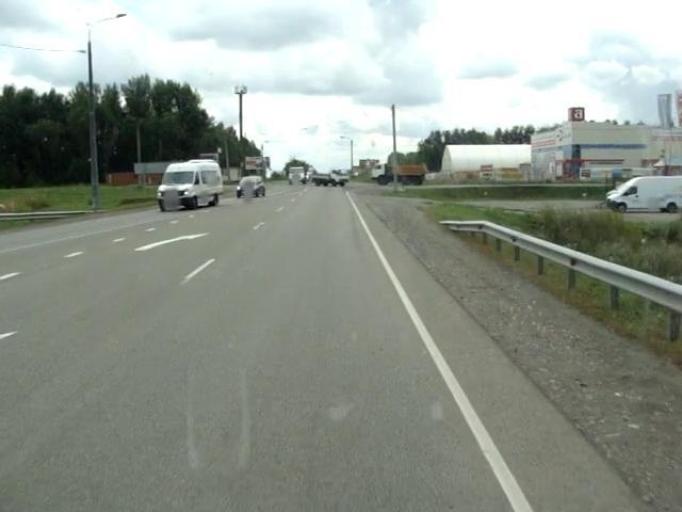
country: RU
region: Altai Krai
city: Zarya
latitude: 52.5757
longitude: 85.1799
